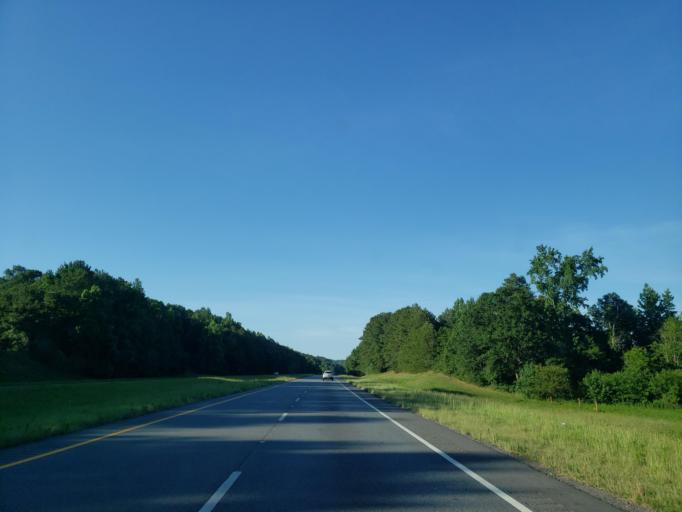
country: US
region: Georgia
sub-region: Floyd County
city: Shannon
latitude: 34.3093
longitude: -85.1116
